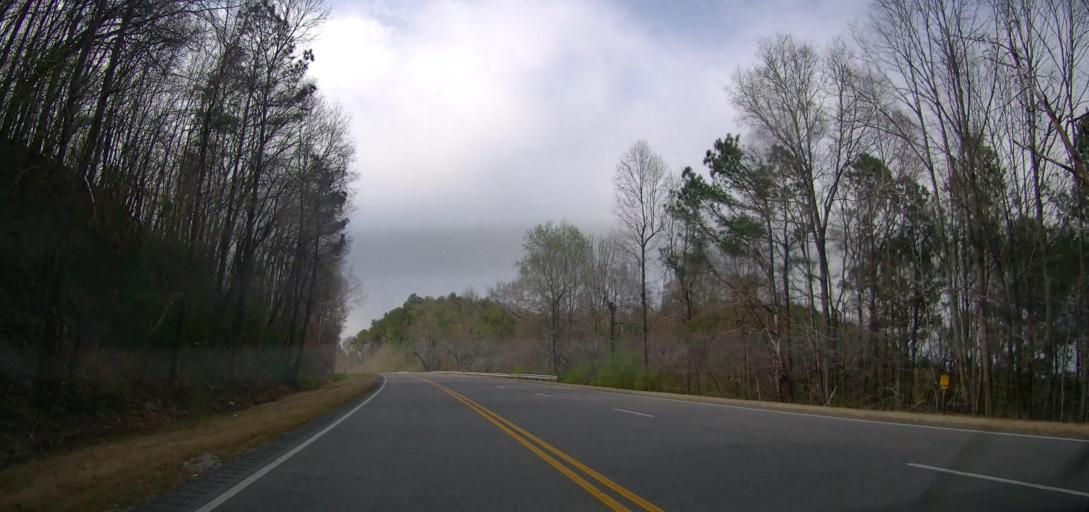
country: US
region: Alabama
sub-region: Walker County
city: Carbon Hill
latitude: 33.9157
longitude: -87.5660
